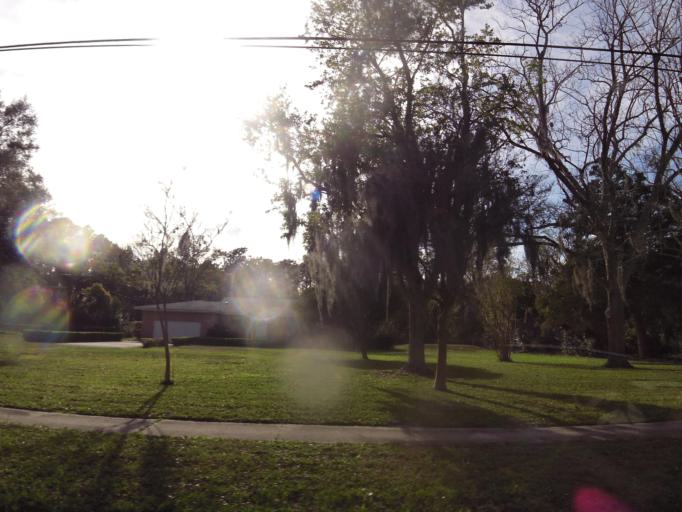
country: US
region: Florida
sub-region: Clay County
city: Bellair-Meadowbrook Terrace
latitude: 30.2376
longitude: -81.7646
